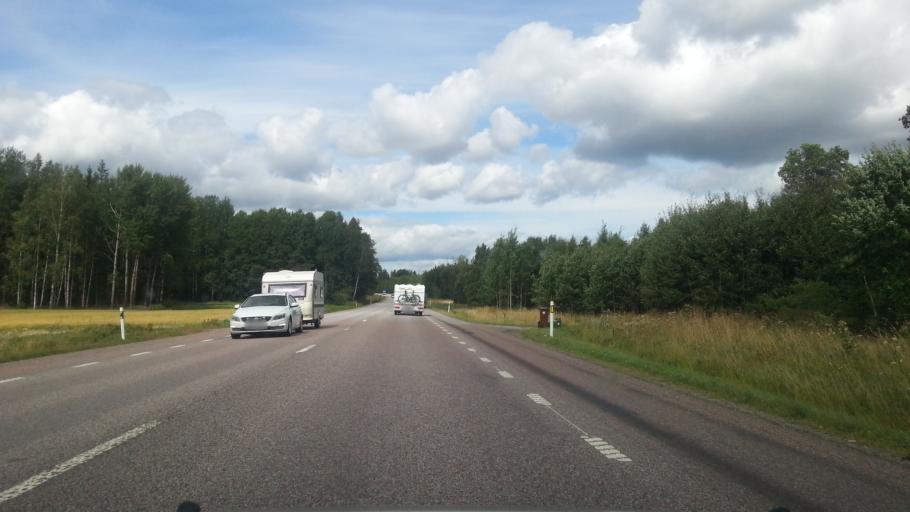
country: SE
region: OErebro
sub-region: Orebro Kommun
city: Hovsta
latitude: 59.4296
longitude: 15.1697
